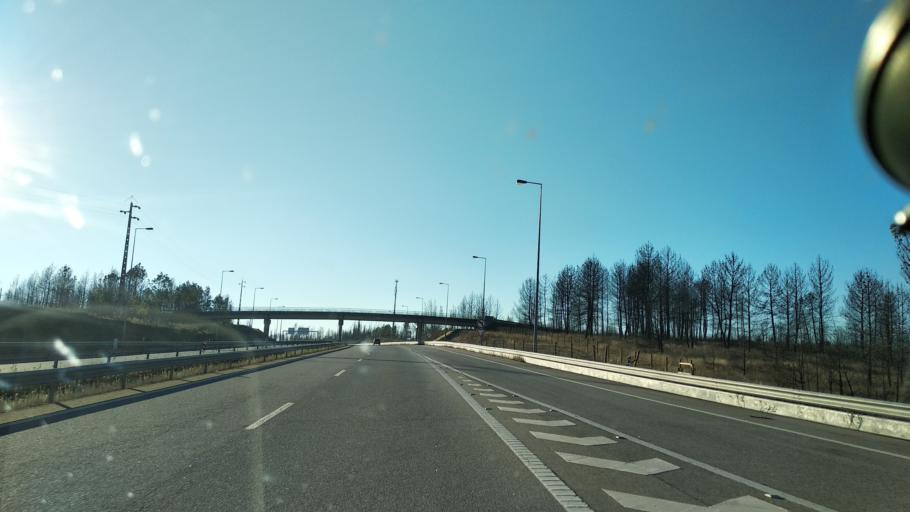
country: PT
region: Santarem
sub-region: Macao
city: Macao
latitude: 39.5298
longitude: -7.9512
